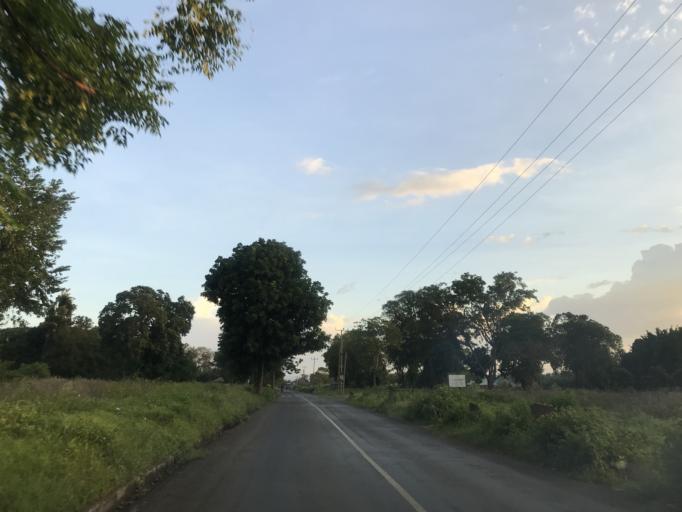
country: TZ
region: Arusha
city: Usa River
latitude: -3.3594
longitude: 36.8668
